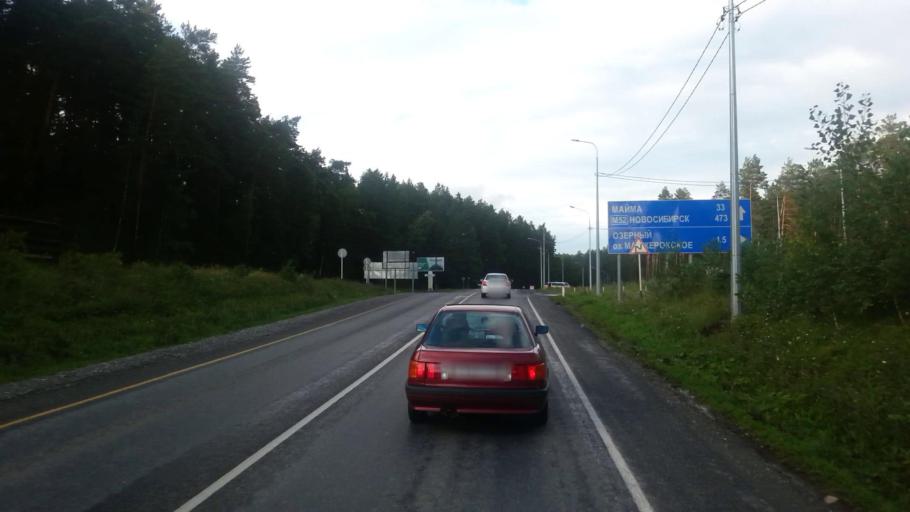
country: RU
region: Altay
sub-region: Mayminskiy Rayon
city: Manzherok
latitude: 51.8207
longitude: 85.7852
